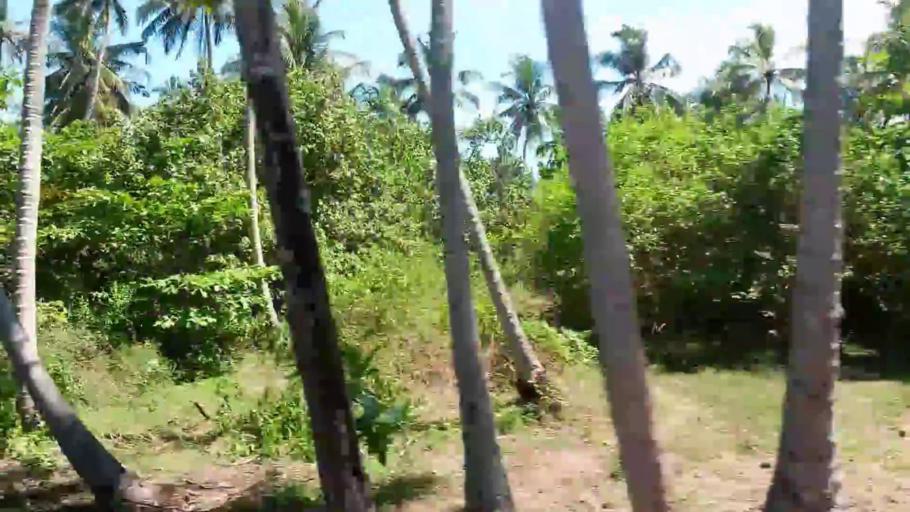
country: LK
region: Southern
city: Hikkaduwa
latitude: 6.1803
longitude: 80.0771
